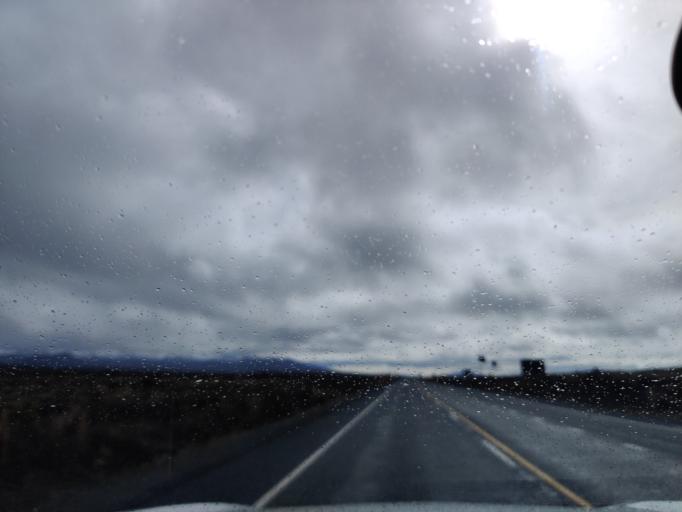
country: NZ
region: Manawatu-Wanganui
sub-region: Ruapehu District
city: Waiouru
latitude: -39.2958
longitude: 175.7410
